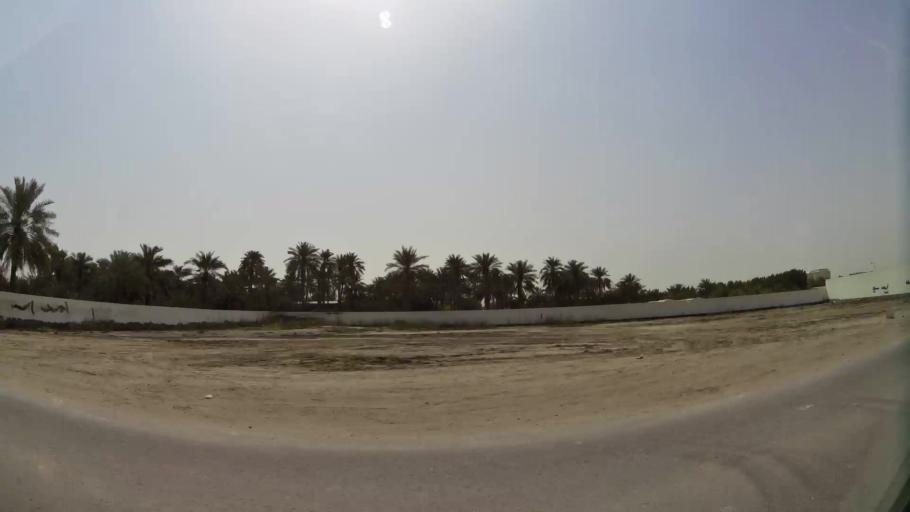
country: BH
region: Manama
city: Jidd Hafs
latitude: 26.2303
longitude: 50.4901
